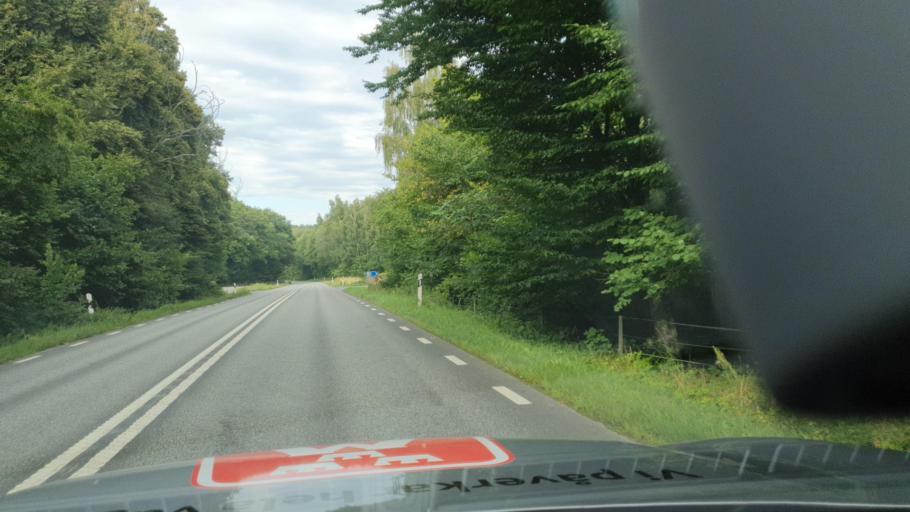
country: SE
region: Skane
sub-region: Bromolla Kommun
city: Bromoella
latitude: 56.1103
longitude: 14.5117
